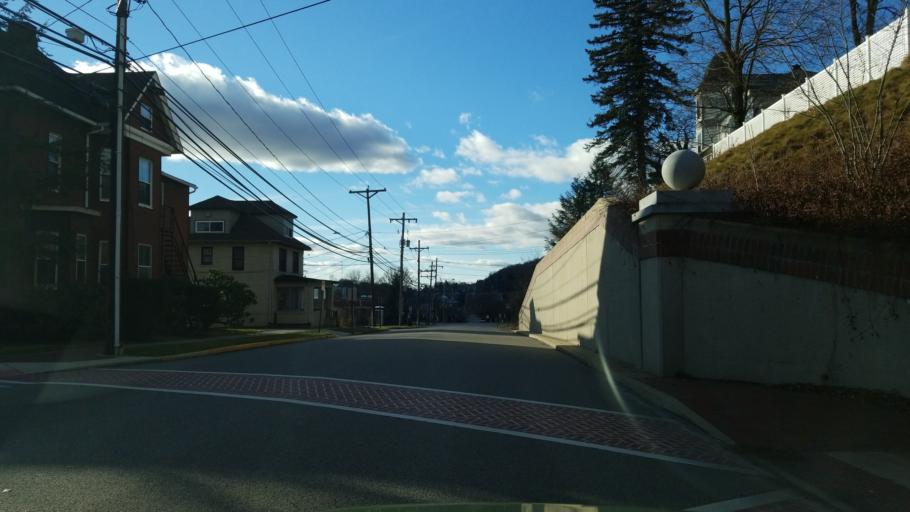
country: US
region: Pennsylvania
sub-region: Indiana County
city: Indiana
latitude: 40.6244
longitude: -79.1533
